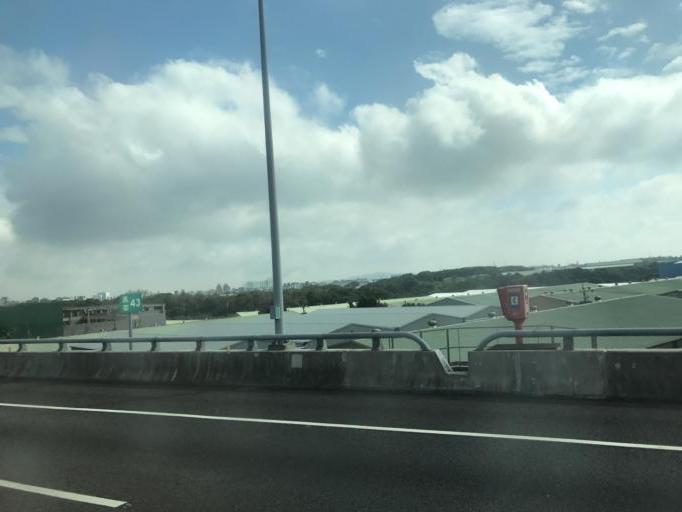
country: TW
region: Taiwan
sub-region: Taoyuan
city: Taoyuan
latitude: 25.0653
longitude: 121.3476
